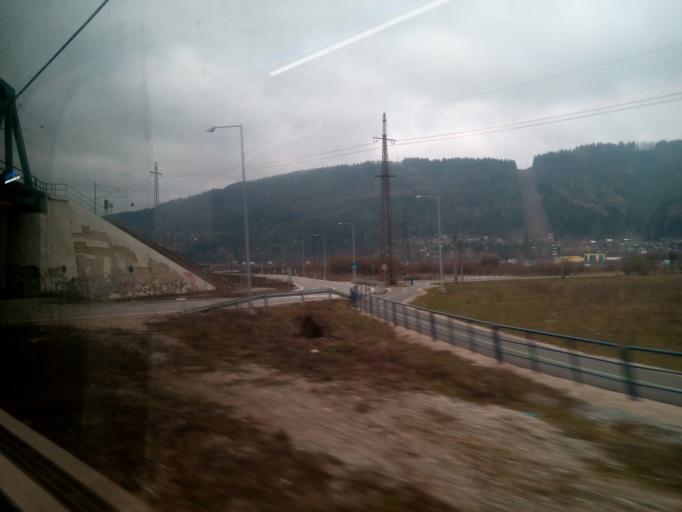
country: SK
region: Zilinsky
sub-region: Okres Zilina
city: Zilina
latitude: 49.2191
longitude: 18.7777
